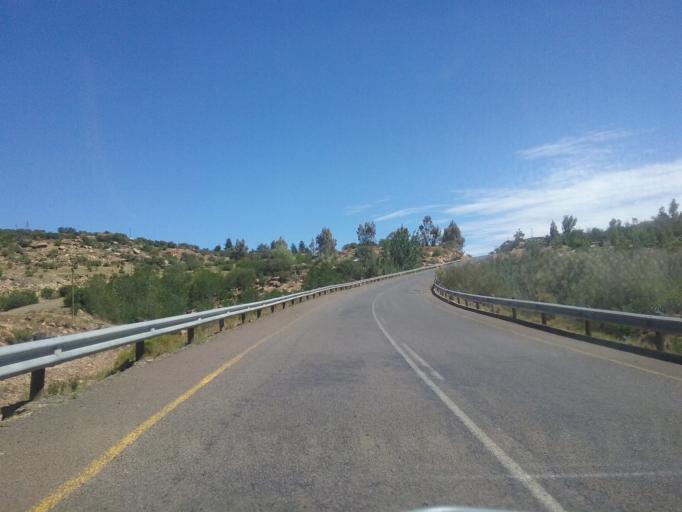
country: LS
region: Quthing
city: Quthing
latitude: -30.3667
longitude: 27.5511
